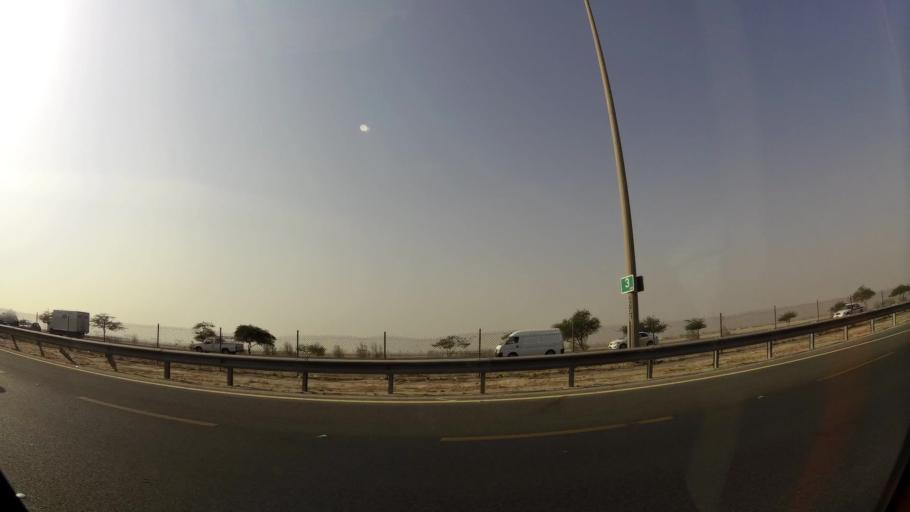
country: KW
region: Mubarak al Kabir
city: Mubarak al Kabir
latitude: 29.1752
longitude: 48.0371
